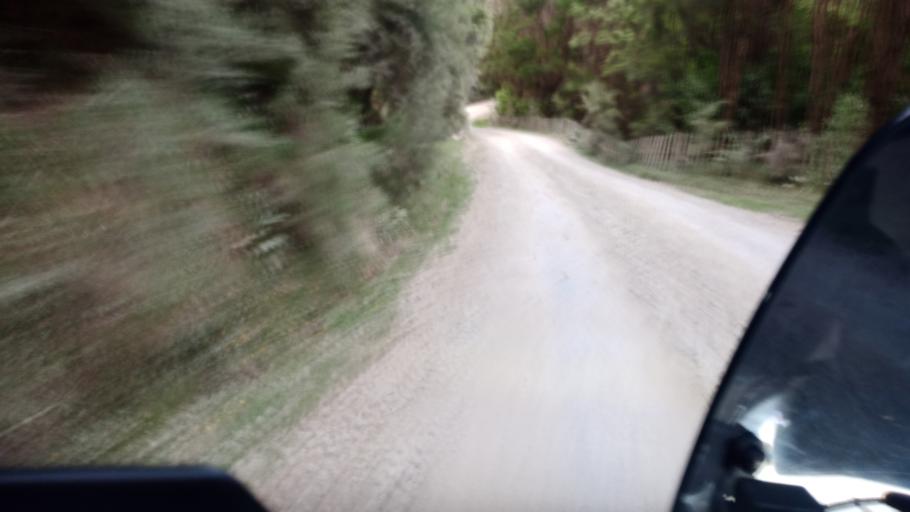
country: NZ
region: Gisborne
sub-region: Gisborne District
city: Gisborne
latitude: -38.4716
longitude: 177.9770
